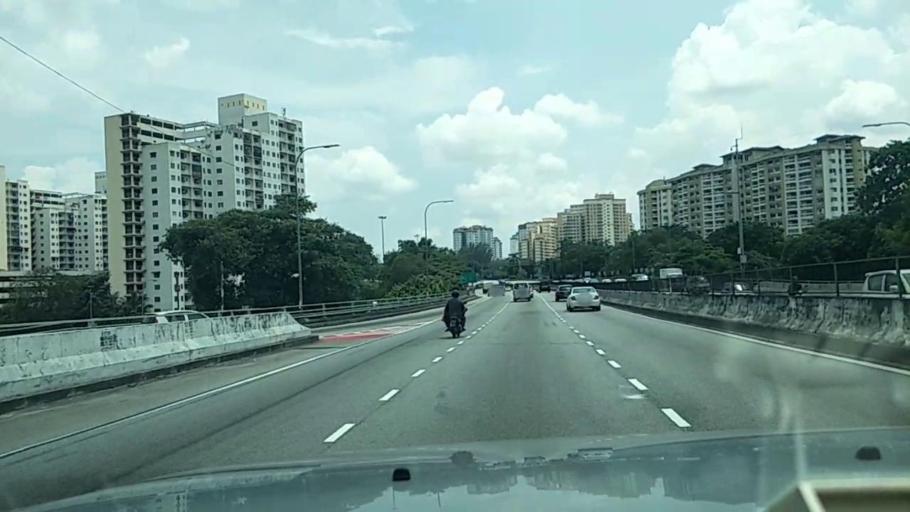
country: MY
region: Selangor
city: Kampong Baharu Balakong
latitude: 3.0665
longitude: 101.7076
